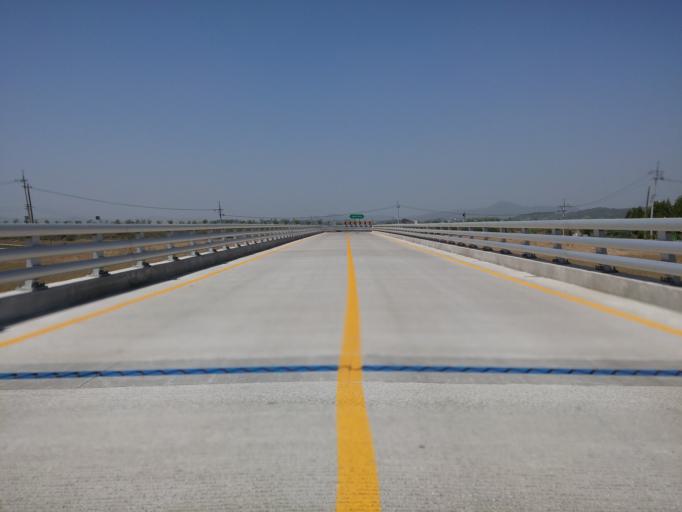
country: KR
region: Chungcheongnam-do
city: Nonsan
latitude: 36.2151
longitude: 127.0993
